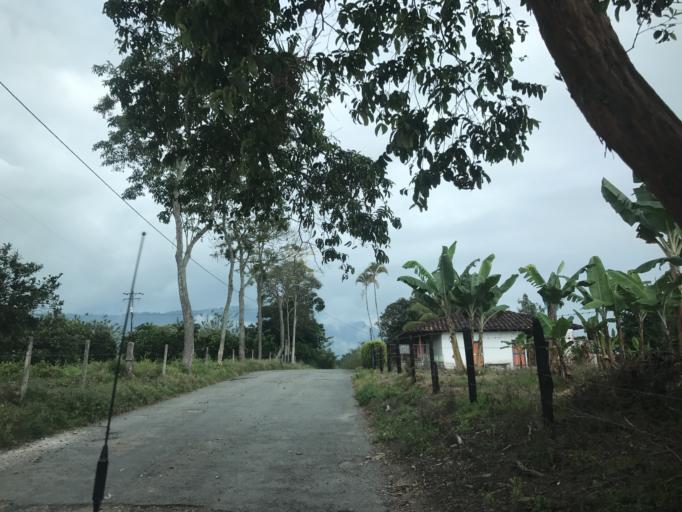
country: CO
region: Quindio
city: Montenegro
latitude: 4.5434
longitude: -75.8623
